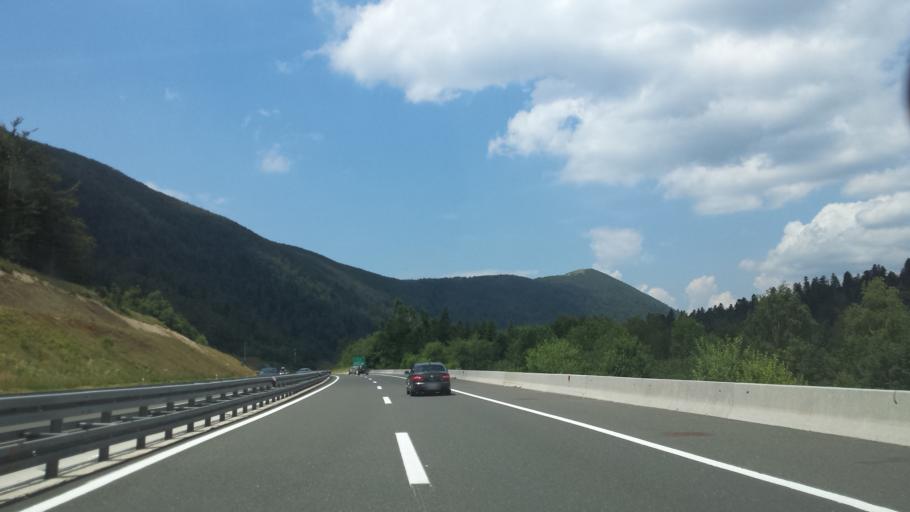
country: HR
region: Primorsko-Goranska
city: Hreljin
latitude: 45.3187
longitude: 14.6738
